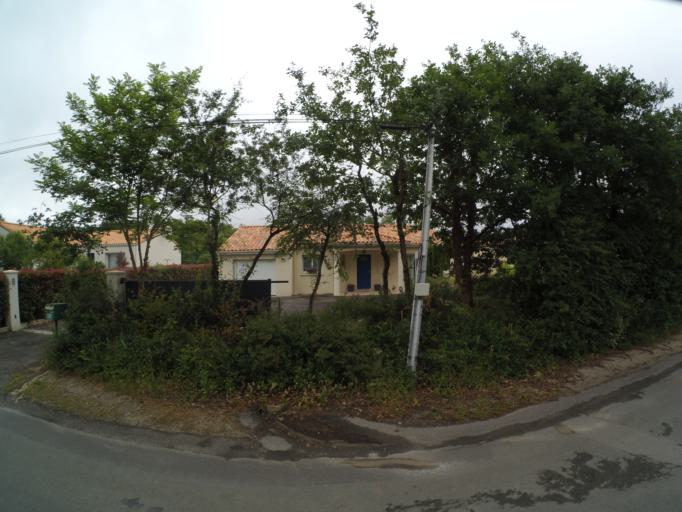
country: FR
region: Pays de la Loire
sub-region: Departement de la Vendee
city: La Roche-sur-Yon
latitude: 46.6339
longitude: -1.4277
